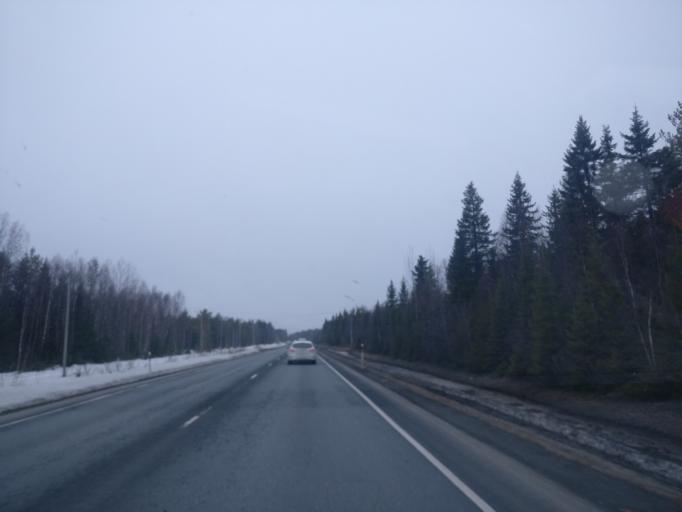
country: FI
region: Lapland
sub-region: Kemi-Tornio
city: Simo
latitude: 65.6715
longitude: 24.9158
